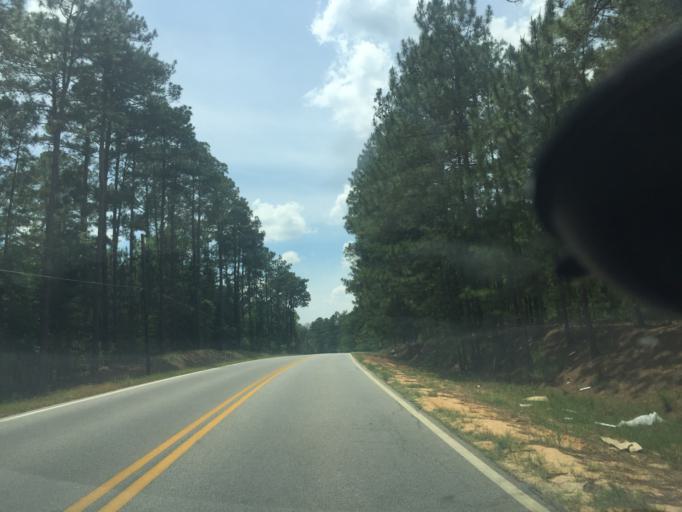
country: US
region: Georgia
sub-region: Bulloch County
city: Statesboro
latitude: 32.4145
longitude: -81.8252
